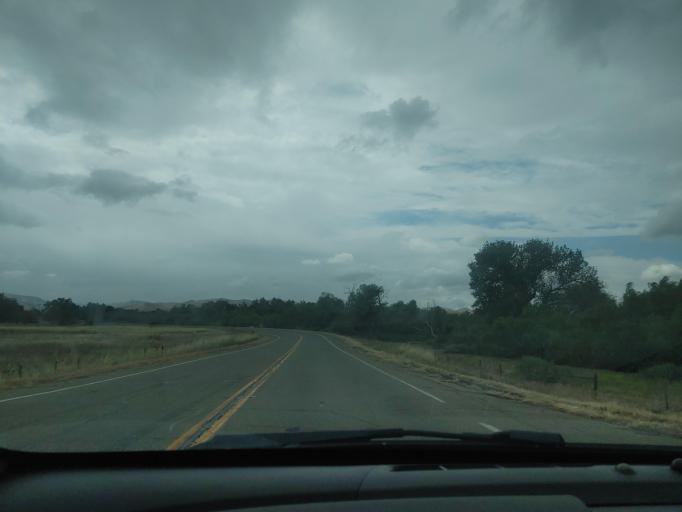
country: US
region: California
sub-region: Stanislaus County
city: Newman
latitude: 37.3298
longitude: -121.1040
